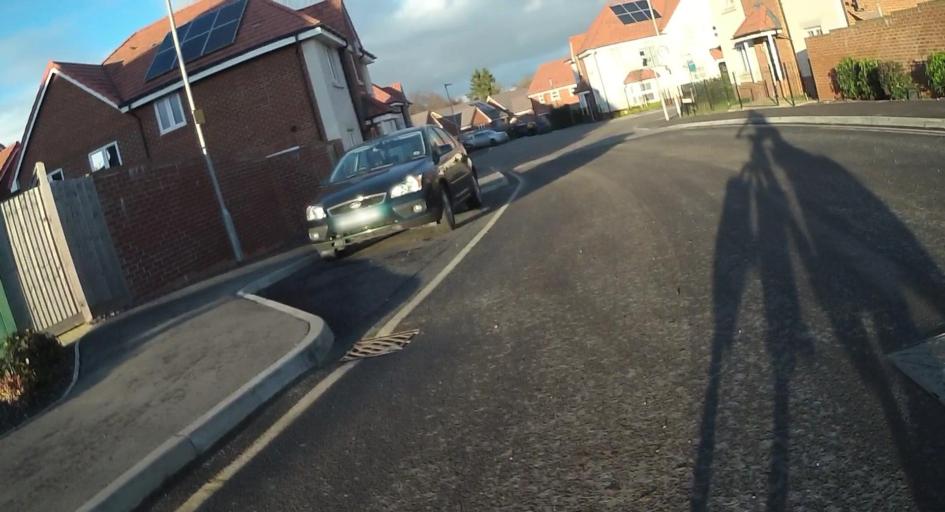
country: GB
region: England
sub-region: Bracknell Forest
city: Binfield
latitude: 51.4159
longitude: -0.7945
